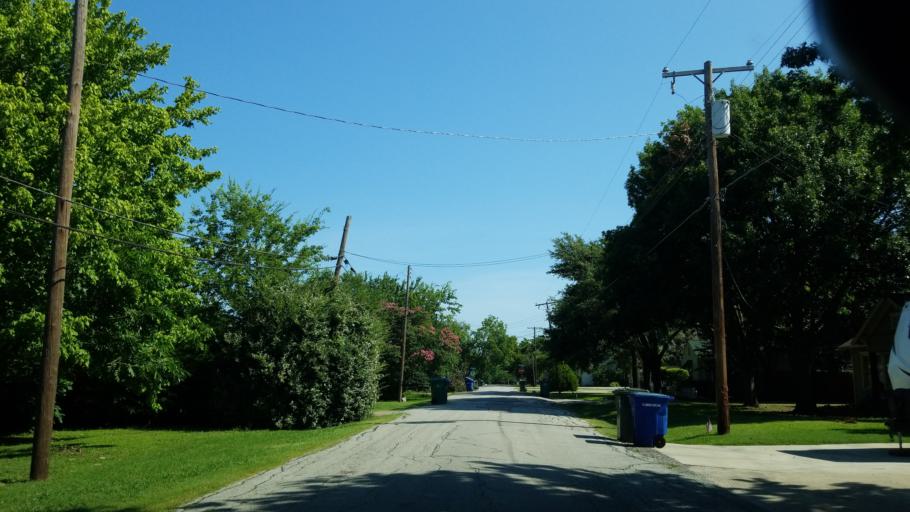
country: US
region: Texas
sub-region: Dallas County
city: Carrollton
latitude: 32.9553
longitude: -96.9002
